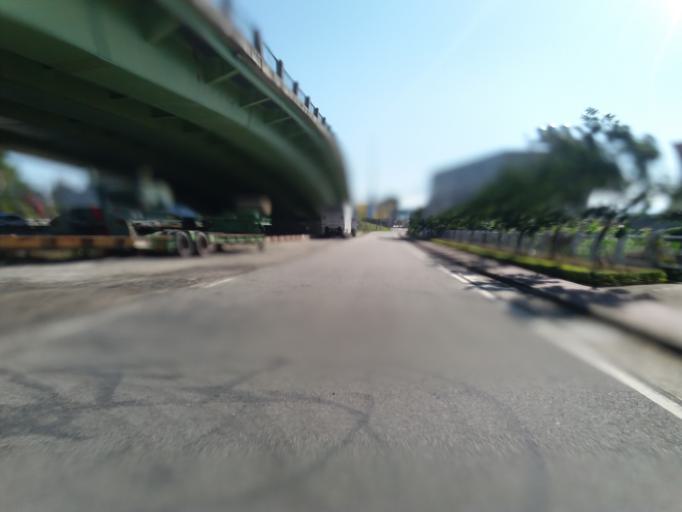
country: TW
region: Taiwan
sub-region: Hsinchu
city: Hsinchu
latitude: 24.7027
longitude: 120.9189
